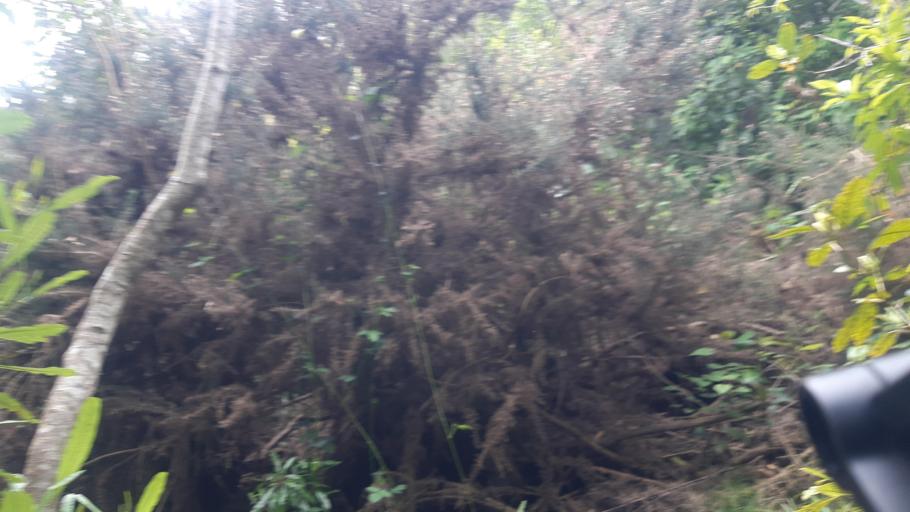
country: NZ
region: Marlborough
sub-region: Marlborough District
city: Picton
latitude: -41.2634
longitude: 174.0015
